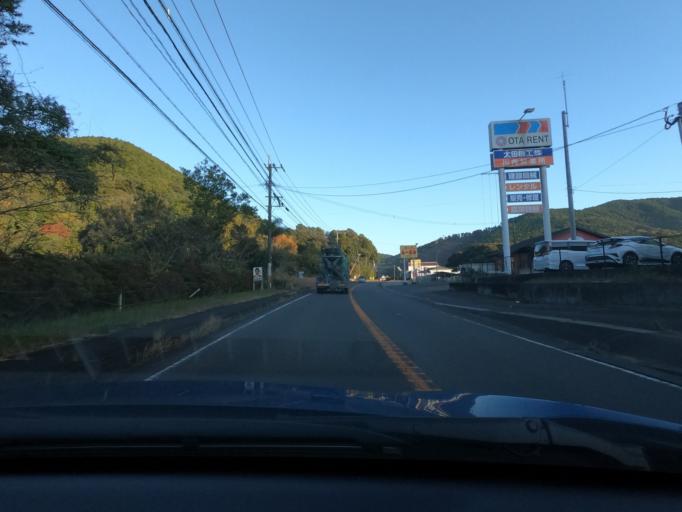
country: JP
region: Kagoshima
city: Satsumasendai
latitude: 31.8053
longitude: 130.3535
